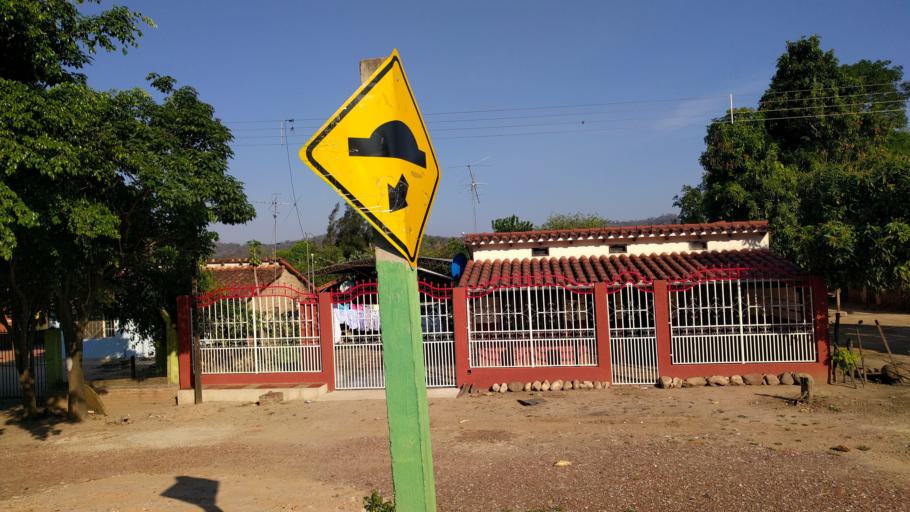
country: BO
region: Santa Cruz
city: Jorochito
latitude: -18.1293
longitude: -63.4684
